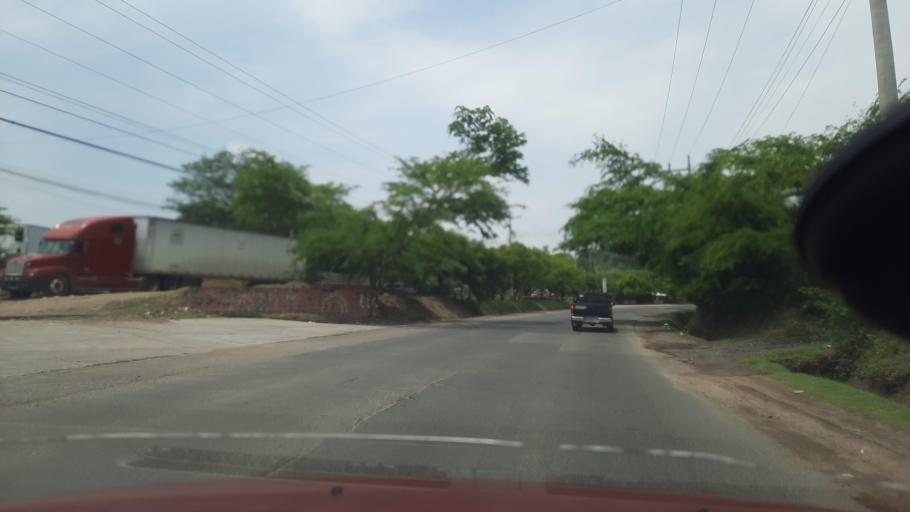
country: SV
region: La Union
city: Santa Rosa de Lima
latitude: 13.6197
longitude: -87.8569
